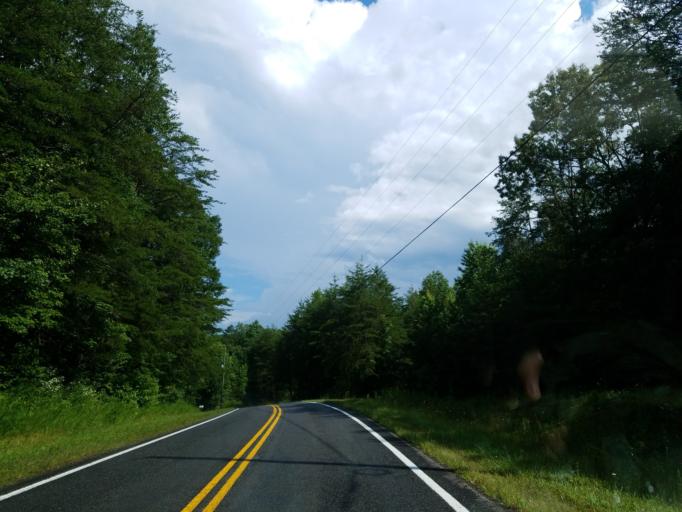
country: US
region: Georgia
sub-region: Fannin County
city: Blue Ridge
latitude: 34.6872
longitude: -84.2986
